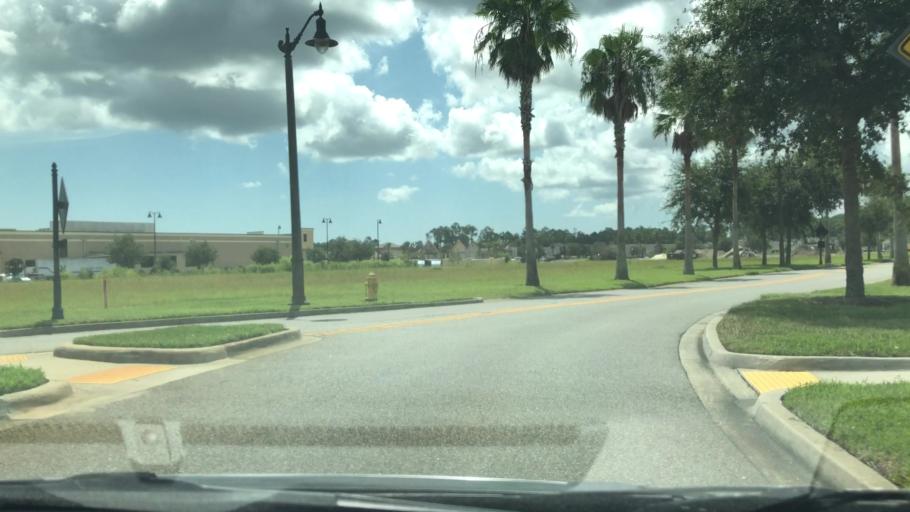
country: US
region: Florida
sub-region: Saint Johns County
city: Palm Valley
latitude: 30.1110
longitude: -81.4214
